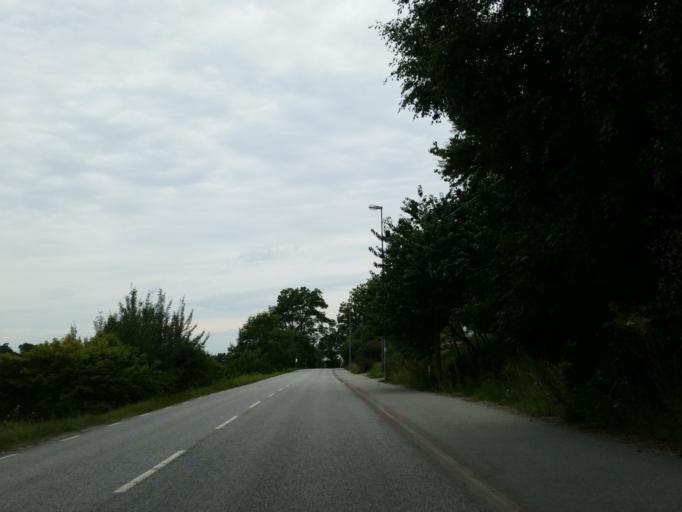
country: SE
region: Stockholm
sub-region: Botkyrka Kommun
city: Eriksberg
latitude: 59.2397
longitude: 17.8151
